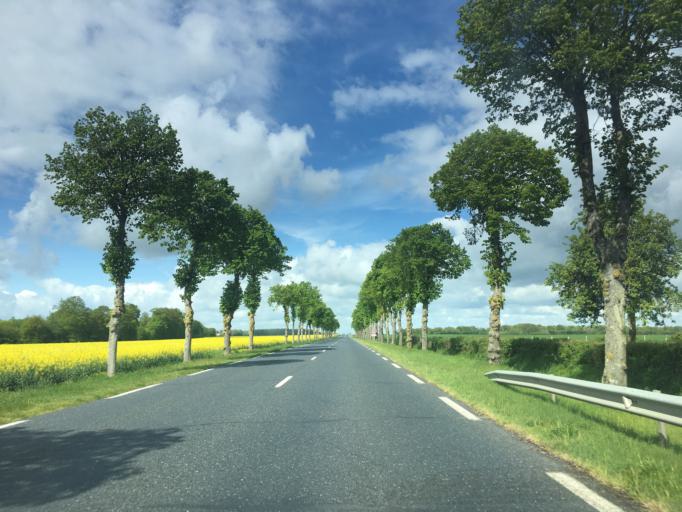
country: FR
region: Haute-Normandie
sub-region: Departement de l'Eure
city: Francheville
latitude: 48.7428
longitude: 0.8604
